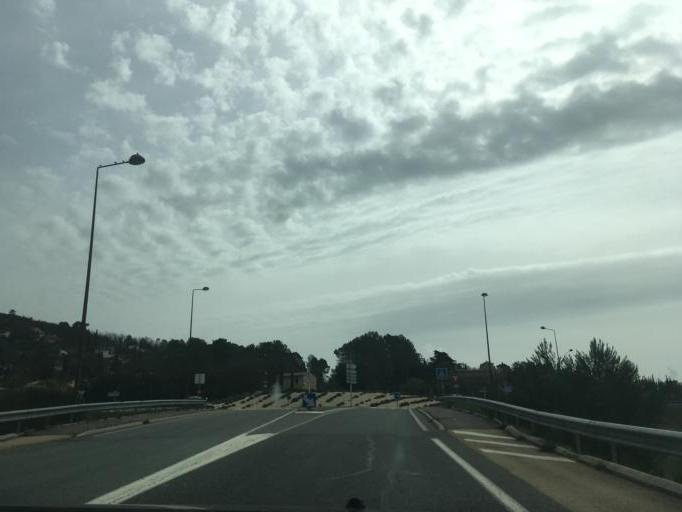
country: FR
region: Provence-Alpes-Cote d'Azur
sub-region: Departement du Var
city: Montauroux
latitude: 43.5996
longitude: 6.7849
